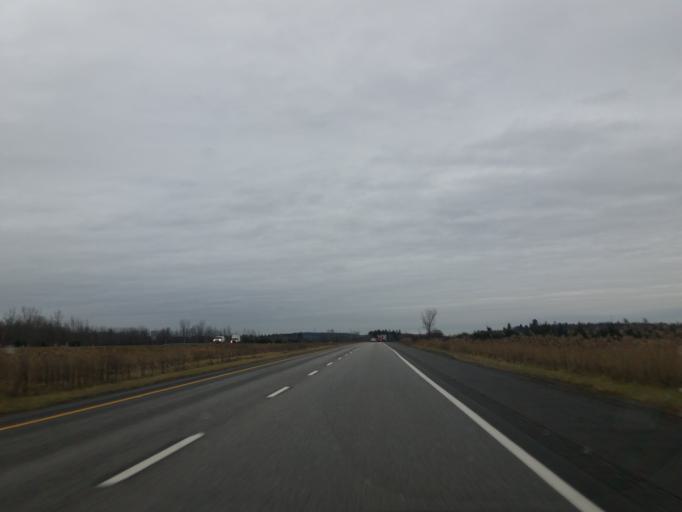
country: CA
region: Quebec
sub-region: Capitale-Nationale
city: Saint-Marc-des-Carrieres
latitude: 46.6766
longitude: -71.9310
